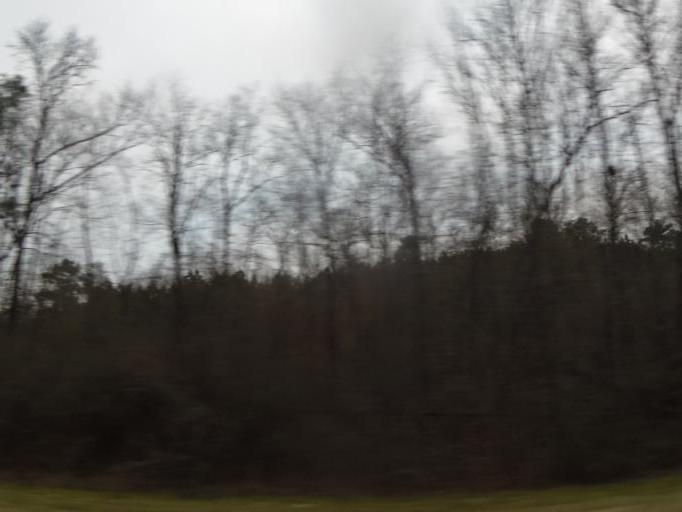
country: US
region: Alabama
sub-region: Blount County
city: Smoke Rise
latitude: 33.9821
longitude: -86.8602
